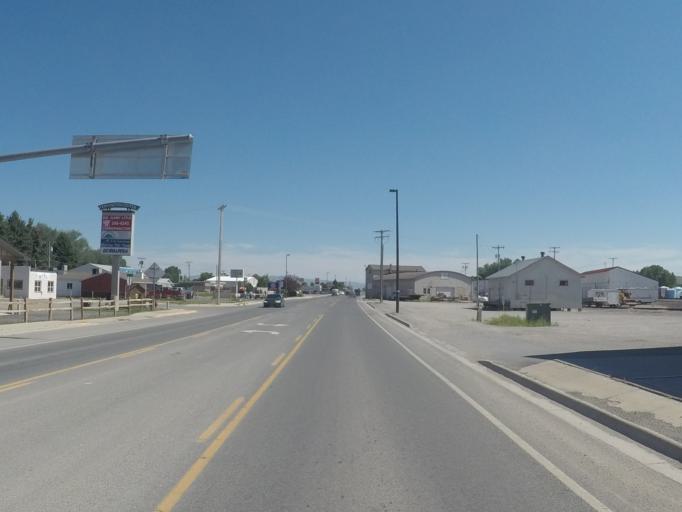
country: US
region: Montana
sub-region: Broadwater County
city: Townsend
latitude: 46.3185
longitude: -111.5210
